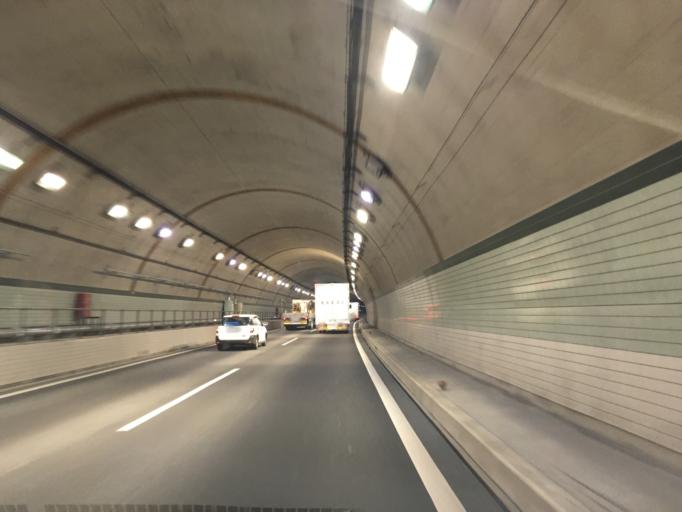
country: JP
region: Tokyo
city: Hachioji
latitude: 35.6373
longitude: 139.2570
